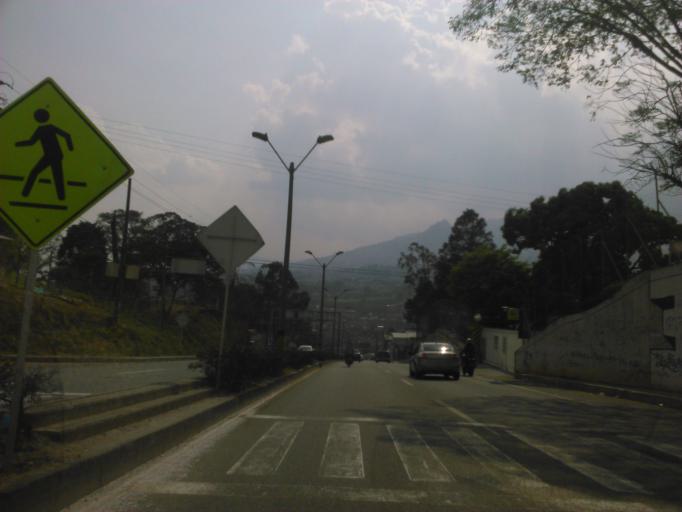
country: CO
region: Antioquia
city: Bello
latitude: 6.3109
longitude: -75.5513
